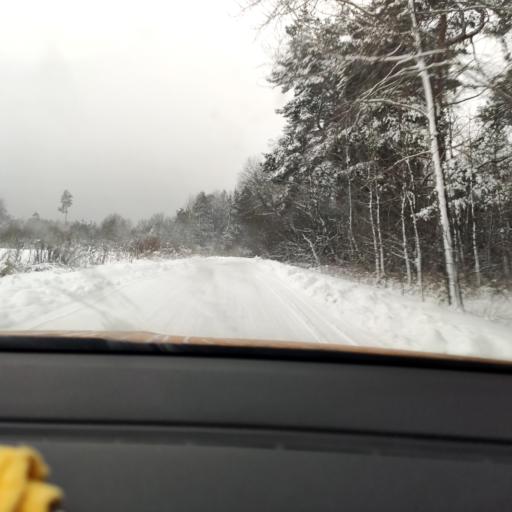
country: RU
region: Moskovskaya
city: Yershovo
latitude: 55.7885
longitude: 36.7801
